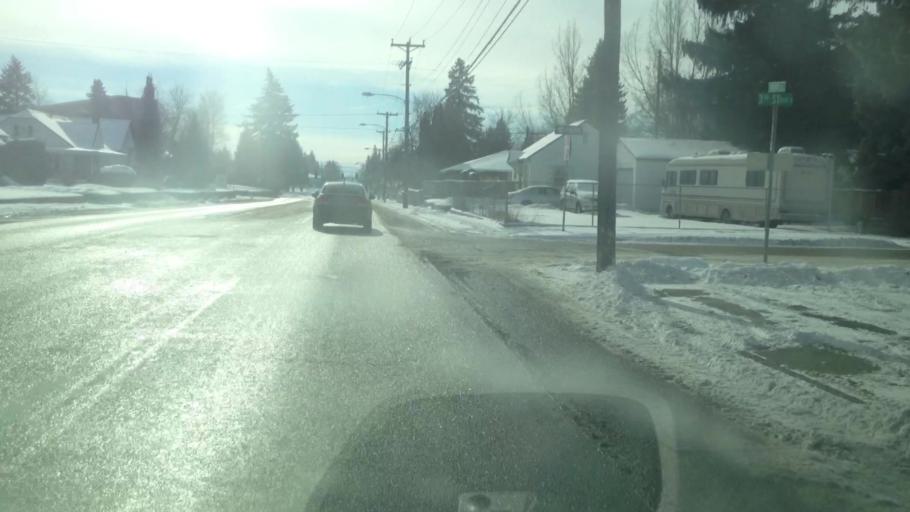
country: US
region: Idaho
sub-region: Bonneville County
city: Idaho Falls
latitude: 43.4953
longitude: -112.0239
